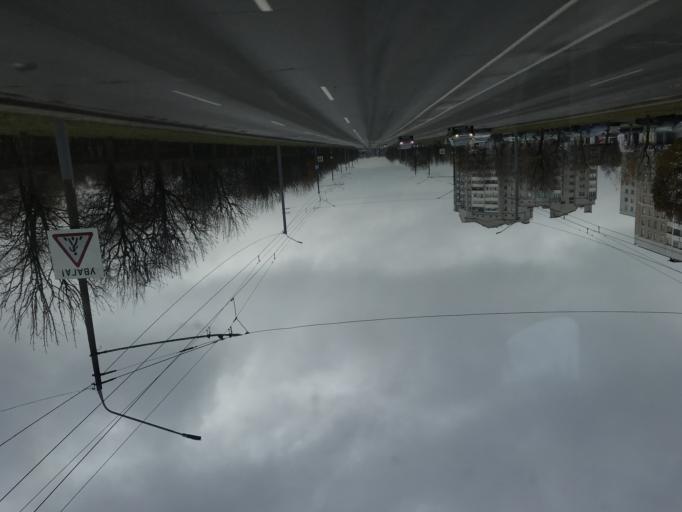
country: BY
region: Mogilev
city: Mahilyow
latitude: 53.8666
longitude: 30.3297
